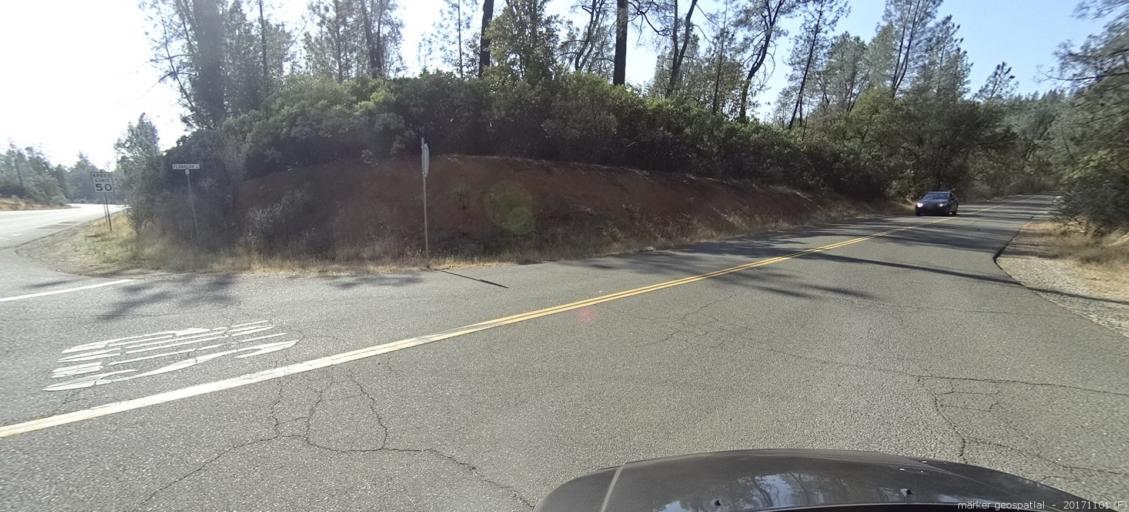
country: US
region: California
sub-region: Shasta County
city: Central Valley (historical)
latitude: 40.6751
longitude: -122.4018
